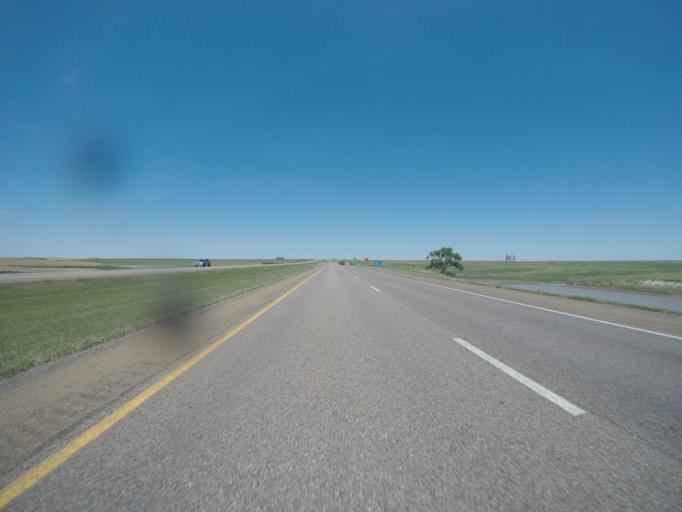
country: US
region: Kansas
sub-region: Thomas County
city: Colby
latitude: 39.3355
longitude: -101.0061
